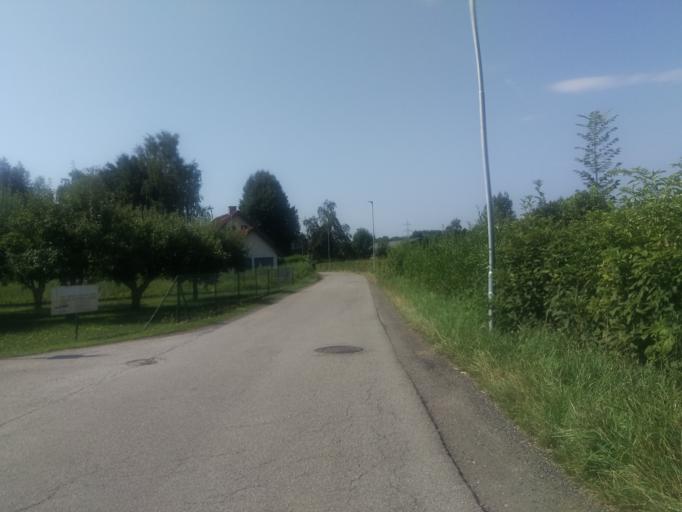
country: AT
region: Styria
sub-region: Politischer Bezirk Graz-Umgebung
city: Gossendorf
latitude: 46.9814
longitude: 15.4909
